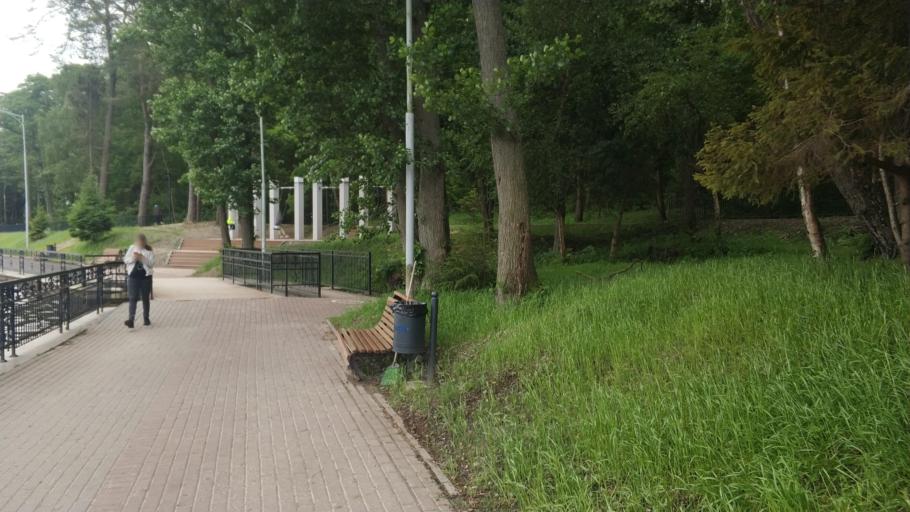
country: RU
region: Kaliningrad
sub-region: Gorod Svetlogorsk
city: Svetlogorsk
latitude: 54.9377
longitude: 20.1512
